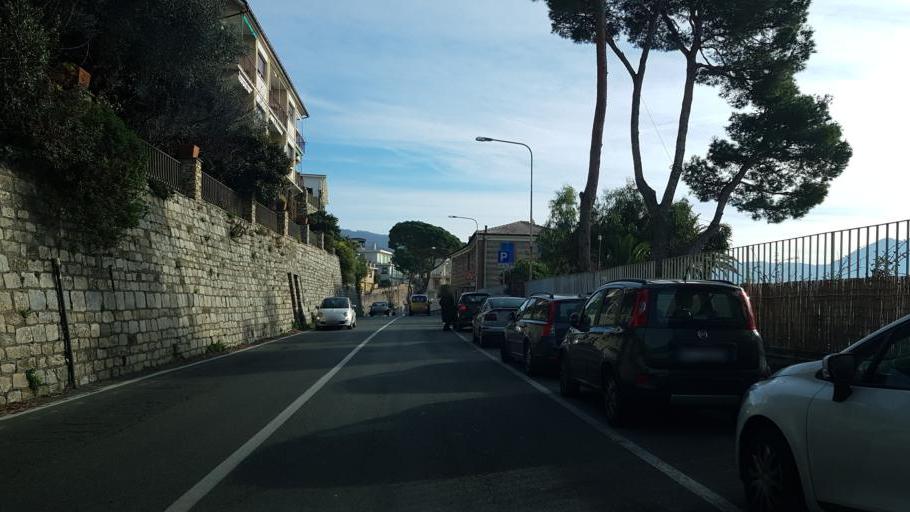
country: IT
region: Liguria
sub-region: Provincia di Genova
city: Sori
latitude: 44.3661
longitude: 9.1192
